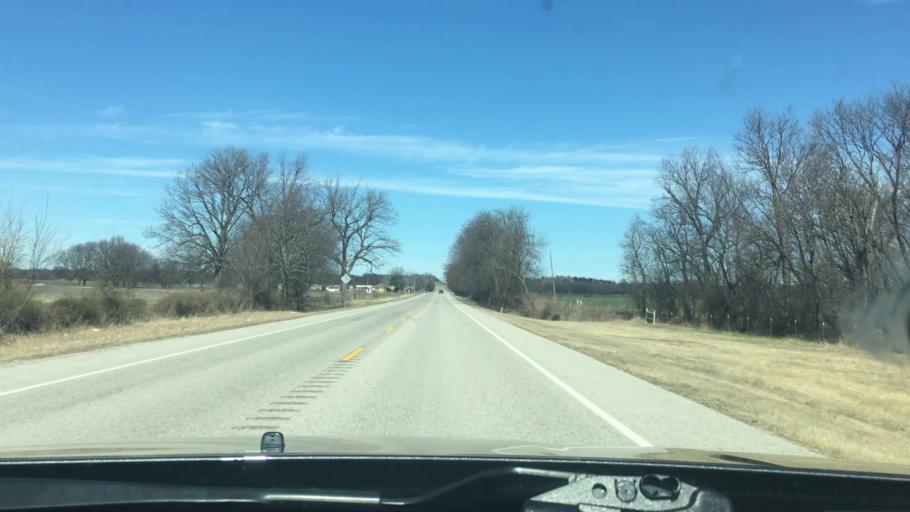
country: US
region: Oklahoma
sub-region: Murray County
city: Sulphur
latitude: 34.3907
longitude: -96.9511
